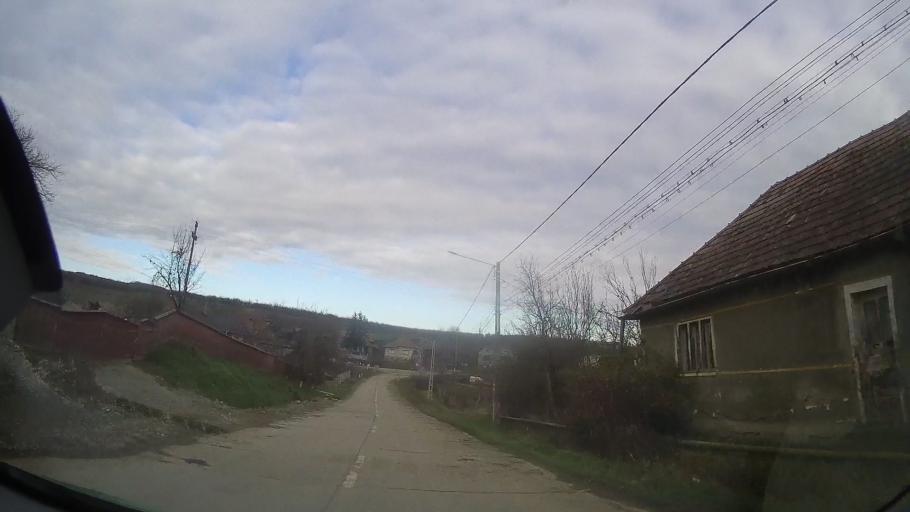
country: RO
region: Bistrita-Nasaud
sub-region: Comuna Sanmihaiu de Campie
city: Sanmihaiu de Campie
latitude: 46.8961
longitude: 24.3368
